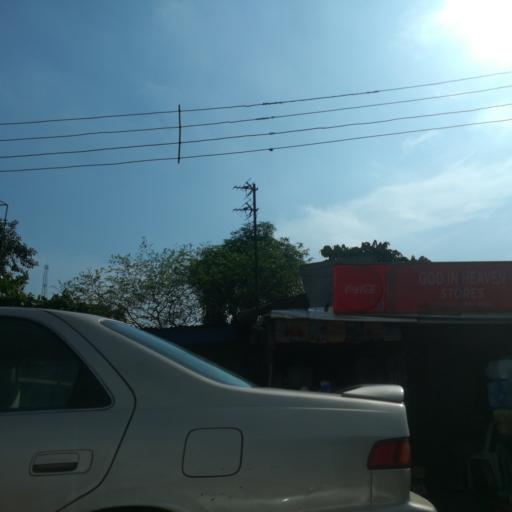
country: NG
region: Rivers
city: Port Harcourt
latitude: 4.8063
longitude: 7.0229
